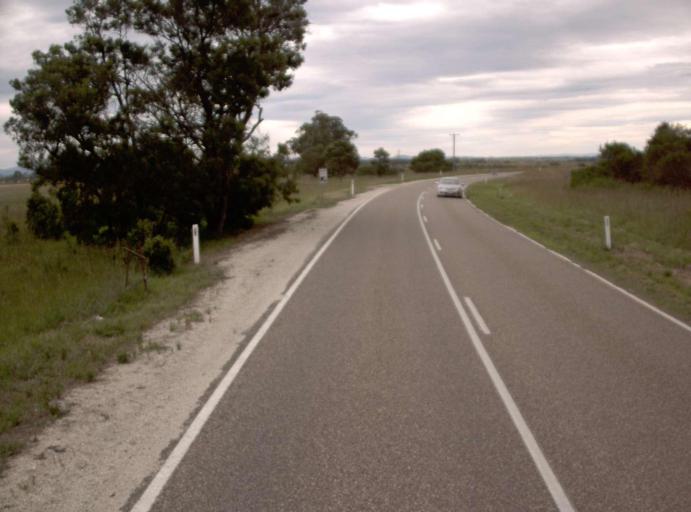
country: AU
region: Victoria
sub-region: Wellington
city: Sale
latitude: -38.0512
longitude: 147.1495
